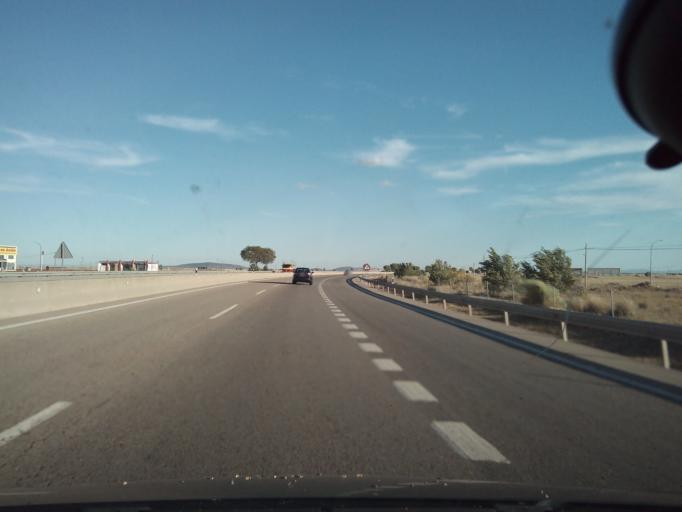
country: ES
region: Castille-La Mancha
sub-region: Province of Toledo
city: Tembleque
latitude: 39.7794
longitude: -3.4798
